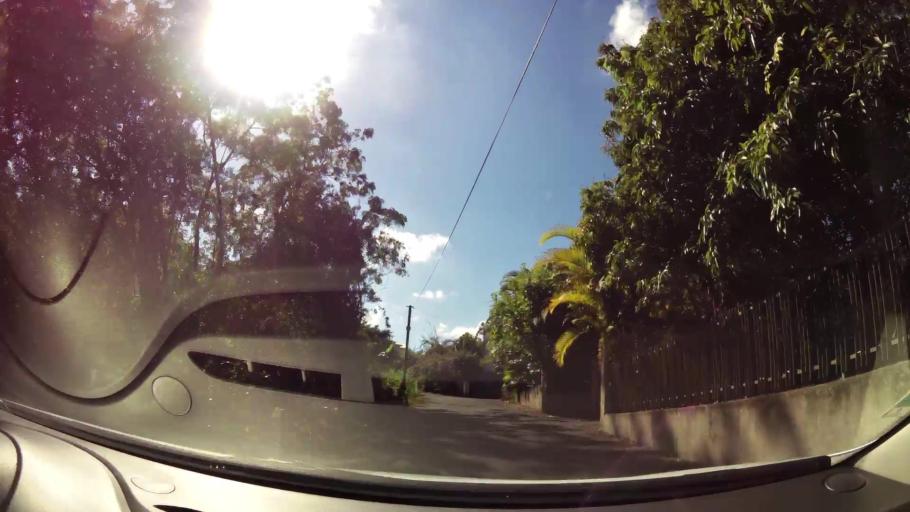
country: RE
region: Reunion
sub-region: Reunion
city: Le Tampon
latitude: -21.2651
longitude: 55.5035
